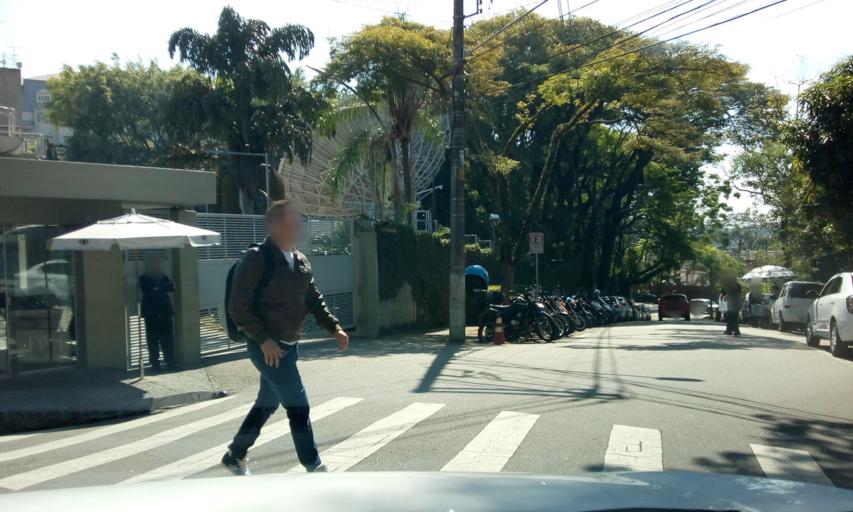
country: BR
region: Sao Paulo
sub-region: Taboao Da Serra
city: Taboao da Serra
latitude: -23.5955
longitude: -46.7096
